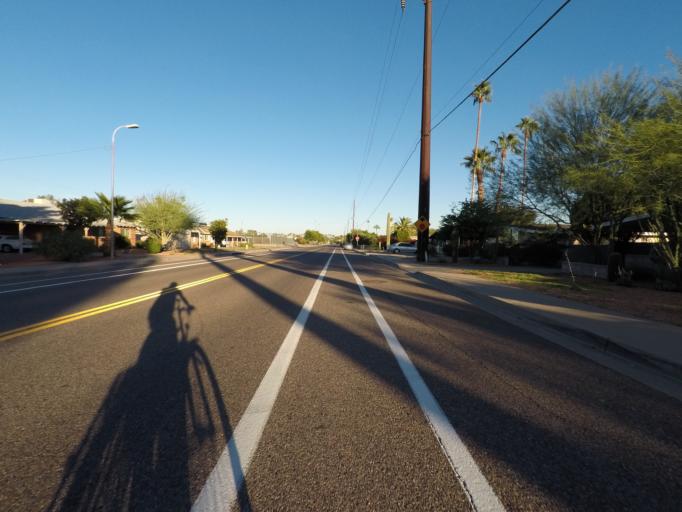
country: US
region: Arizona
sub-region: Maricopa County
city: Scottsdale
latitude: 33.4730
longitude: -111.9230
